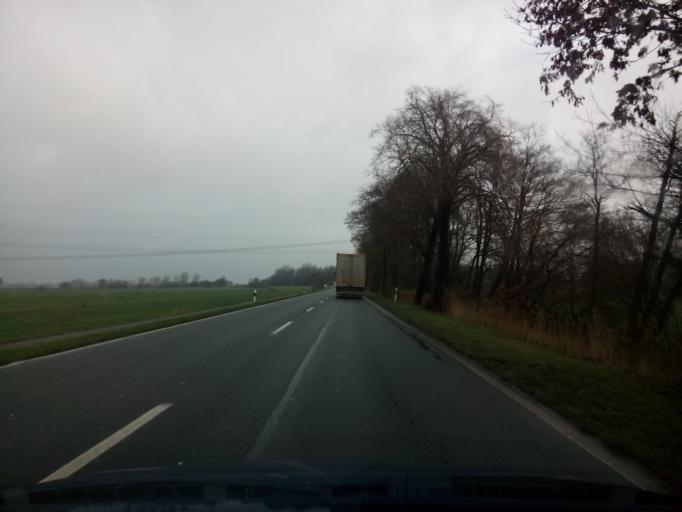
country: DE
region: Lower Saxony
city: Osterholz-Scharmbeck
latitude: 53.1863
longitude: 8.8175
